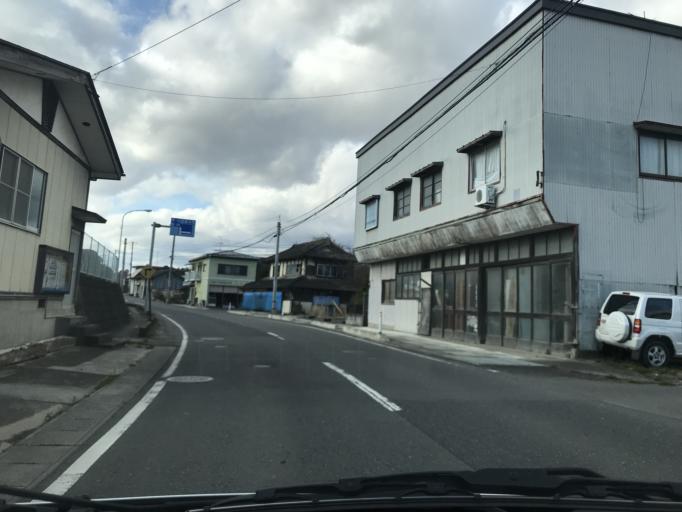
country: JP
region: Miyagi
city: Wakuya
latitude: 38.6281
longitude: 141.2138
